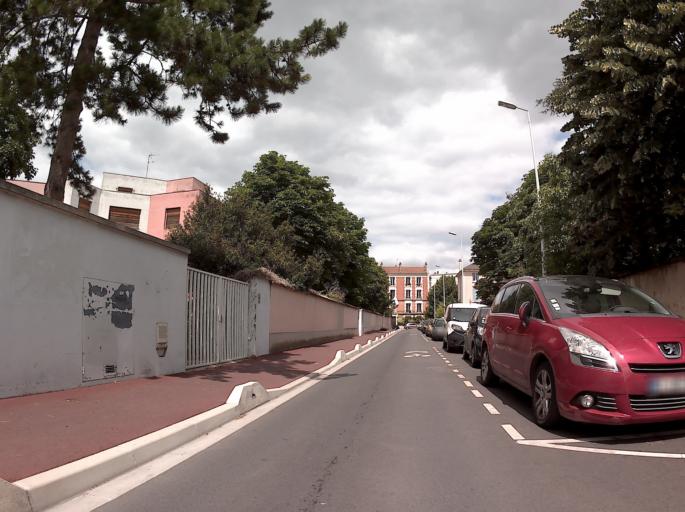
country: FR
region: Ile-de-France
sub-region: Departement des Hauts-de-Seine
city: Rueil-Malmaison
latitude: 48.8897
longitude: 2.1898
